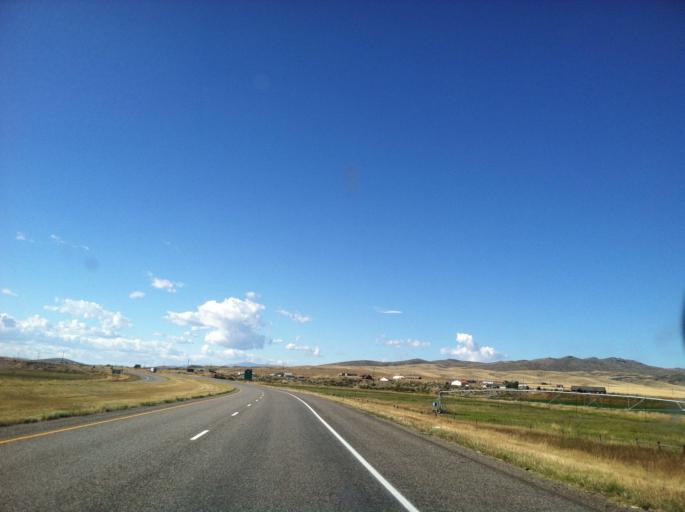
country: US
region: Montana
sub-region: Gallatin County
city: Three Forks
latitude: 45.9117
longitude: -111.5485
